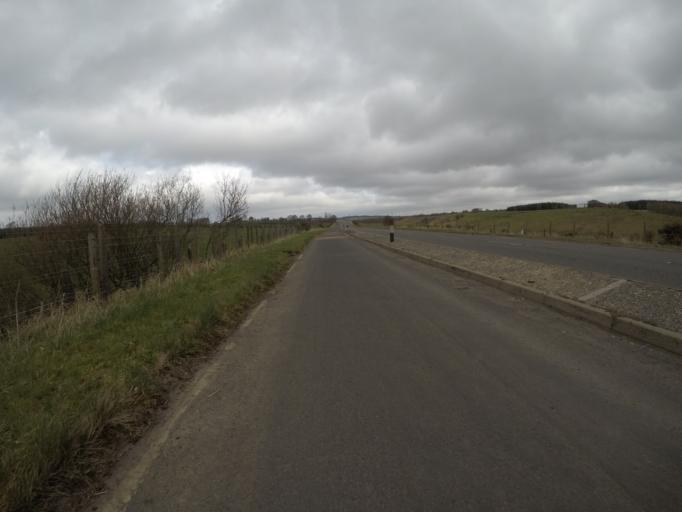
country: GB
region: Scotland
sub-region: East Ayrshire
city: Stewarton
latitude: 55.6766
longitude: -4.4324
